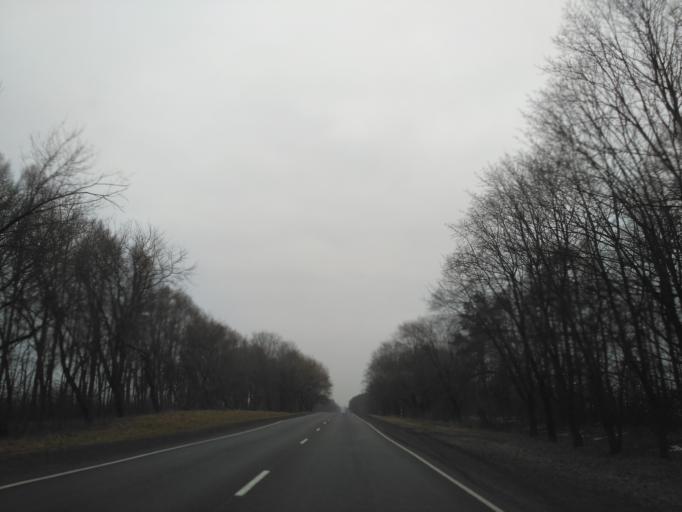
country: BY
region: Brest
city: Baranovichi
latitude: 53.2217
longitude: 26.1686
